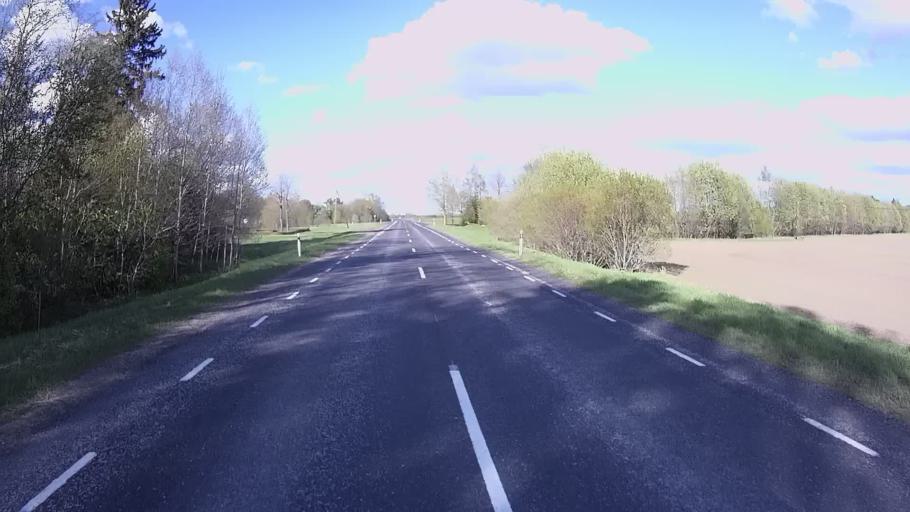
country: EE
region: Jogevamaa
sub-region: Jogeva linn
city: Jogeva
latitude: 58.7168
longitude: 26.1826
